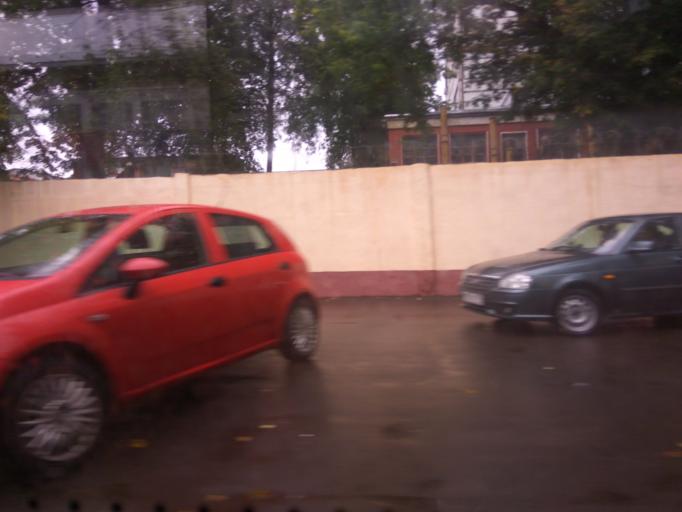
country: RU
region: Moscow
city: Lefortovo
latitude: 55.7840
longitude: 37.7222
